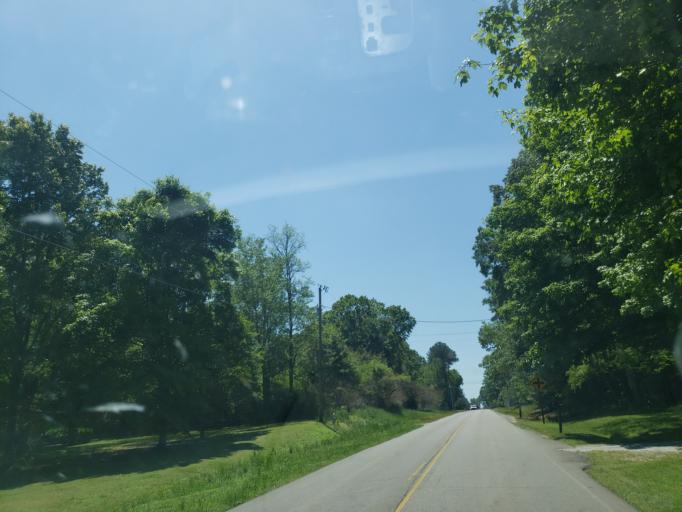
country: US
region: Alabama
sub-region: Madison County
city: Harvest
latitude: 34.8997
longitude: -86.7328
